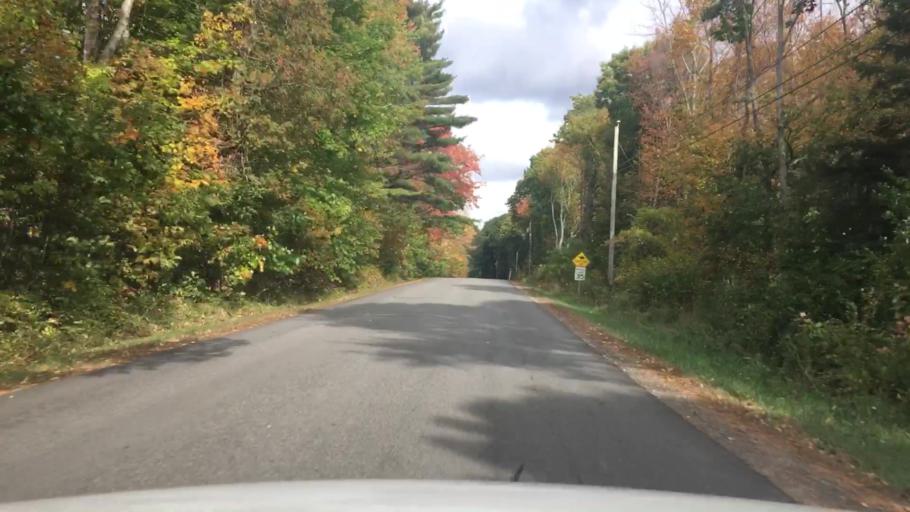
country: US
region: Maine
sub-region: Knox County
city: Camden
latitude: 44.2190
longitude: -69.1015
